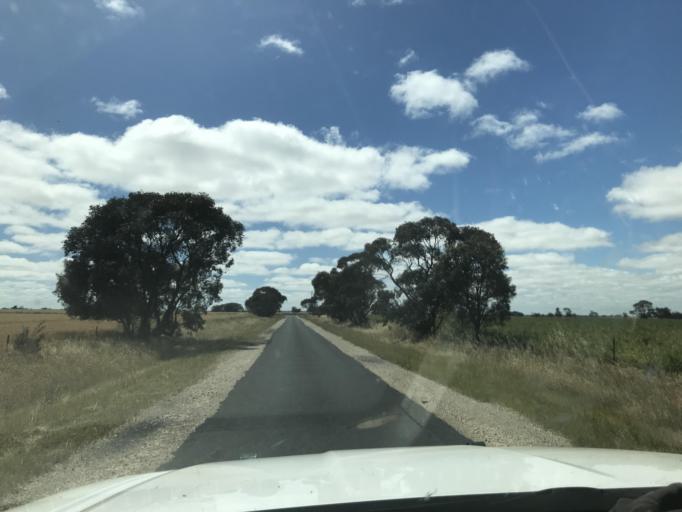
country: AU
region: South Australia
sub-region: Tatiara
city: Bordertown
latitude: -36.2815
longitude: 141.1451
